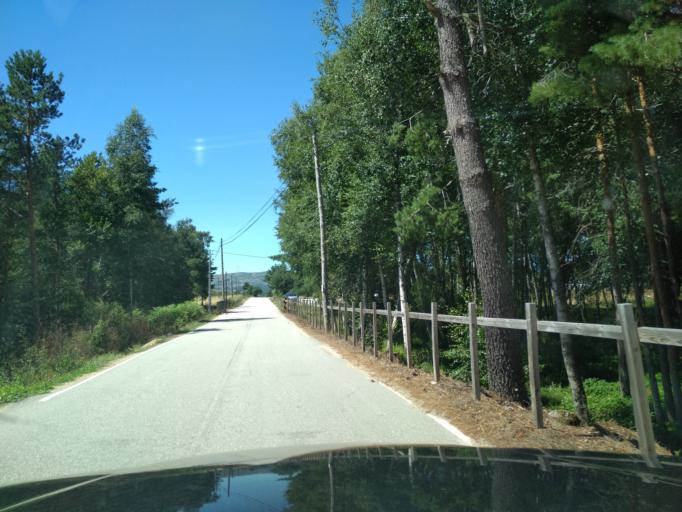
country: PT
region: Vila Real
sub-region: Vila Pouca de Aguiar
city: Vila Pouca de Aguiar
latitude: 41.5034
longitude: -7.6641
